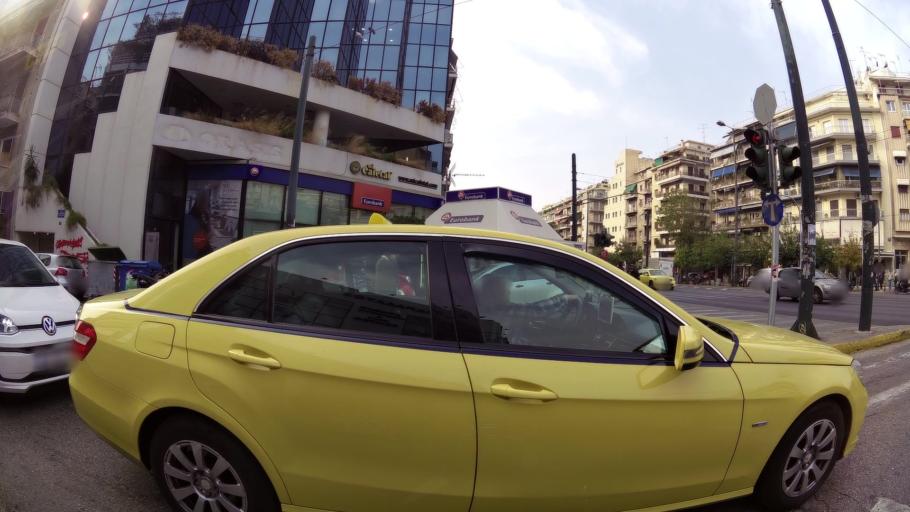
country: GR
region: Attica
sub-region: Nomarchia Athinas
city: Psychiko
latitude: 37.9930
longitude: 23.7670
